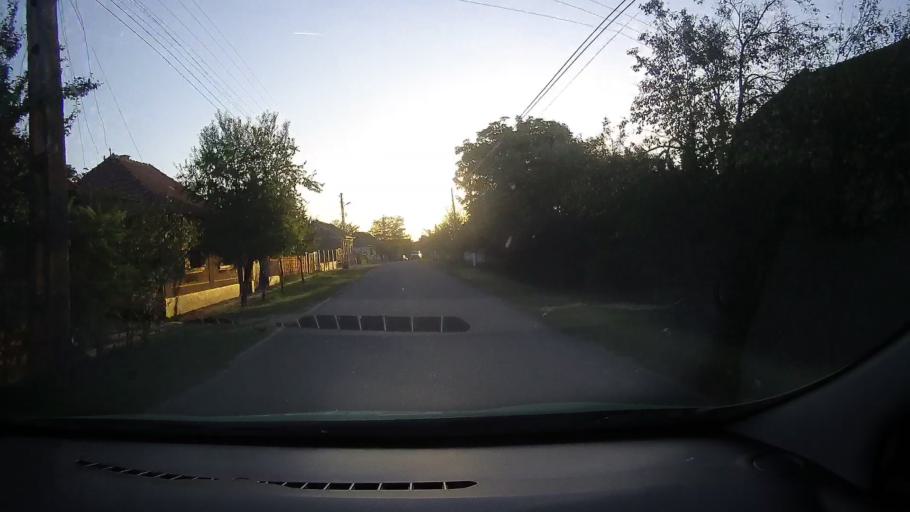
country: RO
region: Bihor
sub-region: Comuna Rosiori
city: Rosiori
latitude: 47.2568
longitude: 21.9608
